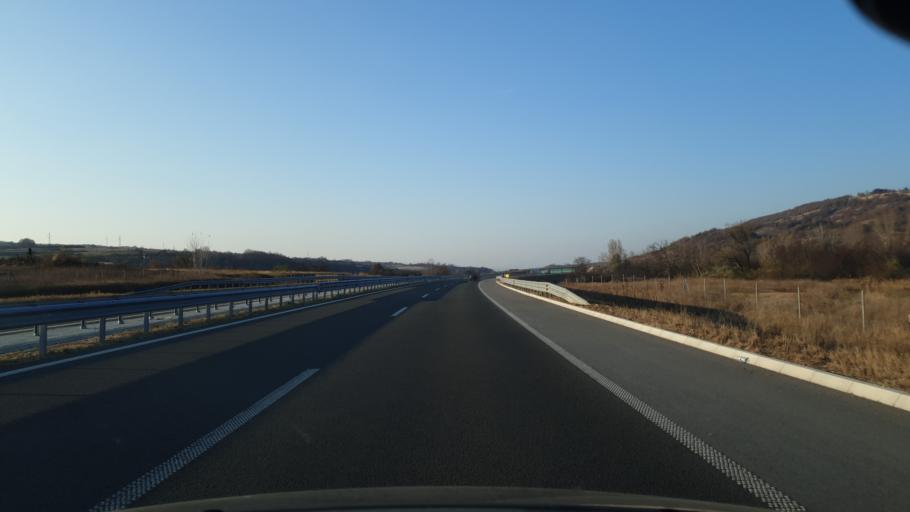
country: RS
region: Central Serbia
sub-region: Pirotski Okrug
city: Dimitrovgrad
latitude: 43.0392
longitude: 22.7120
